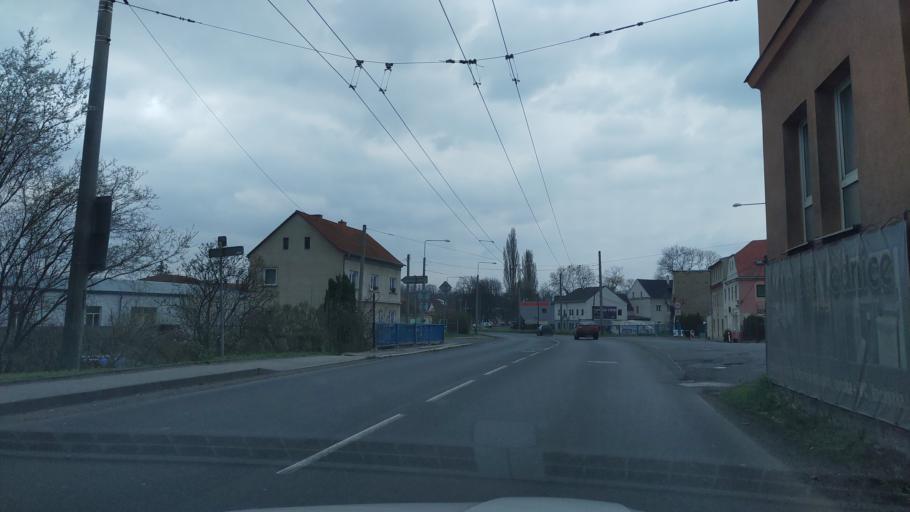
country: CZ
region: Ustecky
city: Trmice
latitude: 50.6580
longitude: 13.9916
